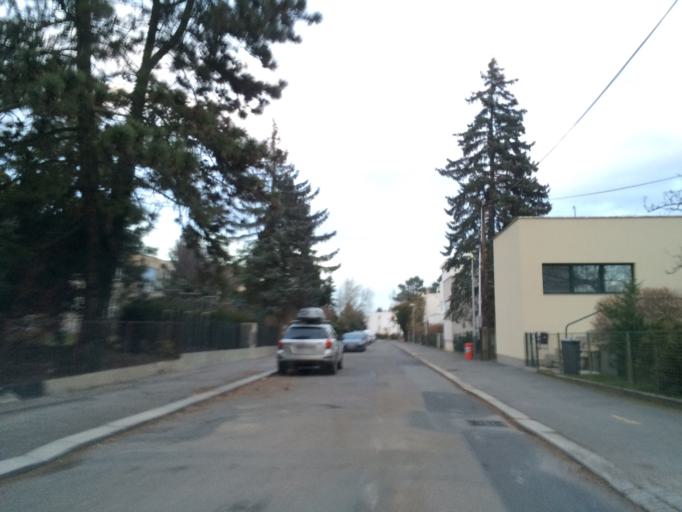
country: CZ
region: Praha
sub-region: Praha 1
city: Mala Strana
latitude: 50.1151
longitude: 14.3853
